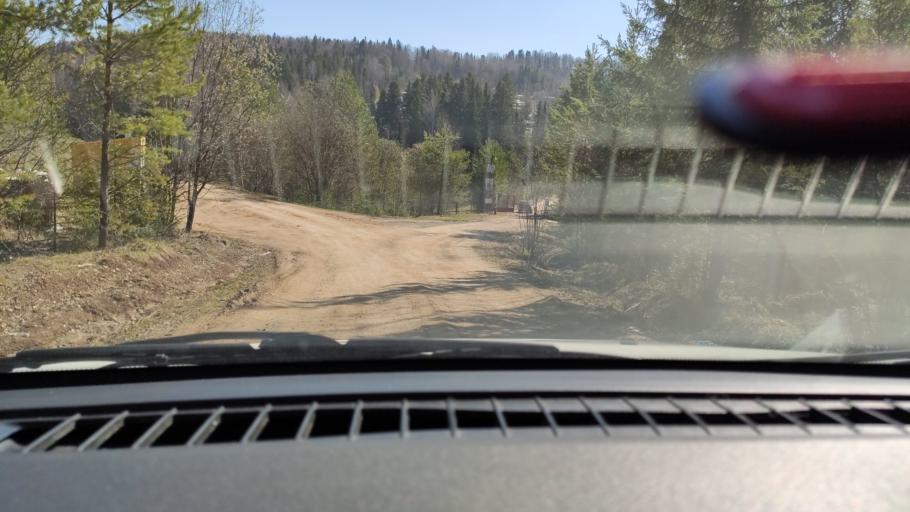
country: RU
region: Perm
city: Bershet'
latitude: 57.7227
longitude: 56.4044
